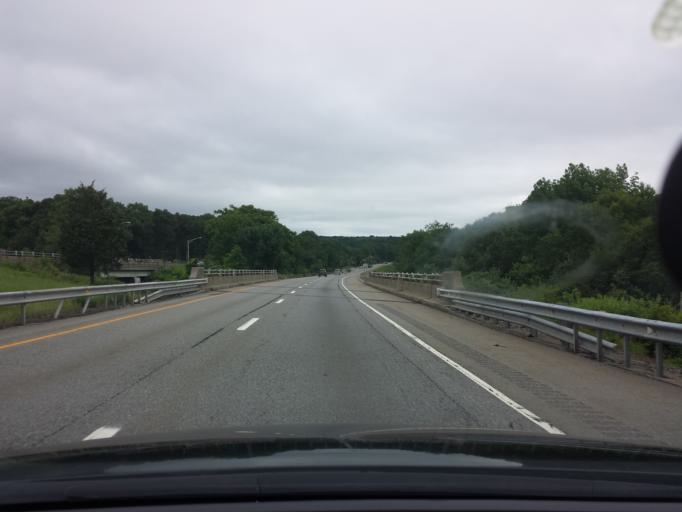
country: US
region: Connecticut
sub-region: New London County
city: Pawcatuck
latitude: 41.4112
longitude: -71.8558
